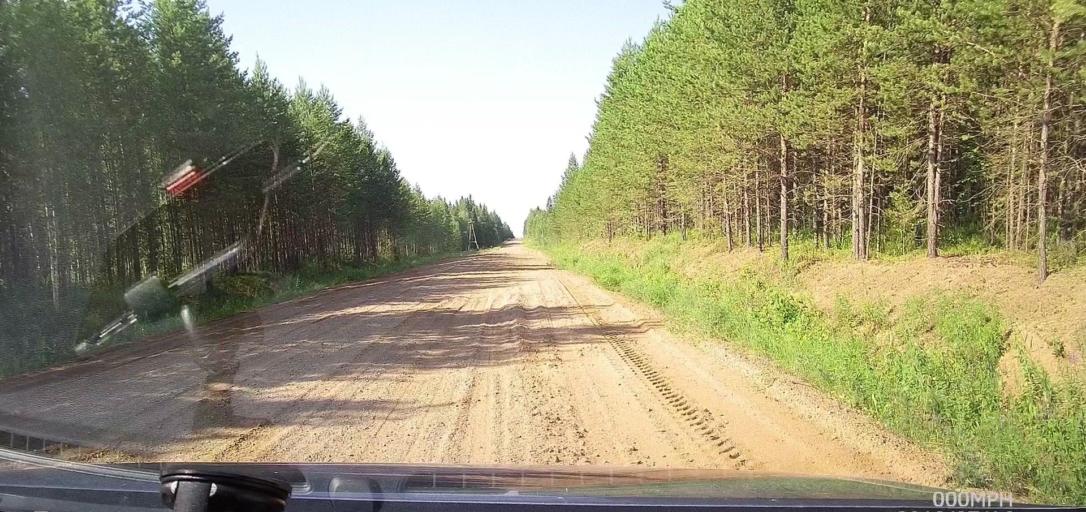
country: RU
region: Arkhangelskaya
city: Mezen'
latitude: 65.4488
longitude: 45.0355
